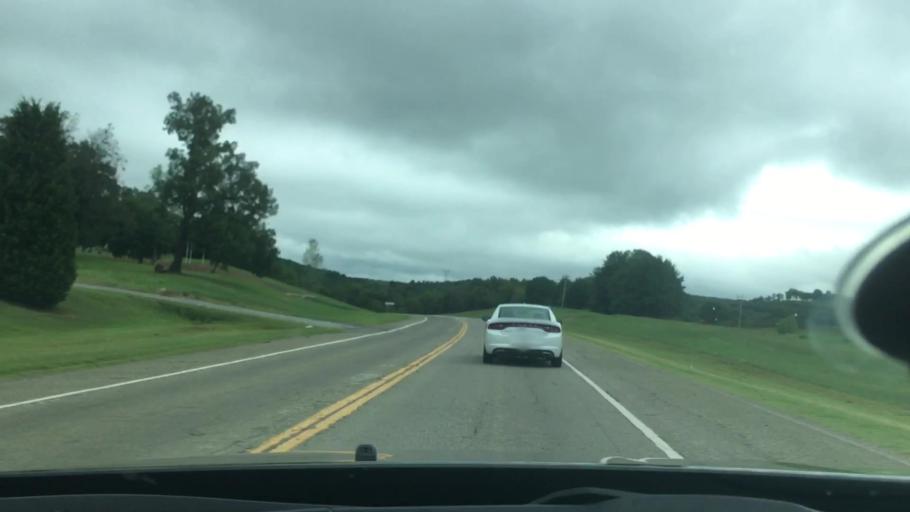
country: US
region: Oklahoma
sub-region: Sequoyah County
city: Vian
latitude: 35.5113
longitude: -94.9688
